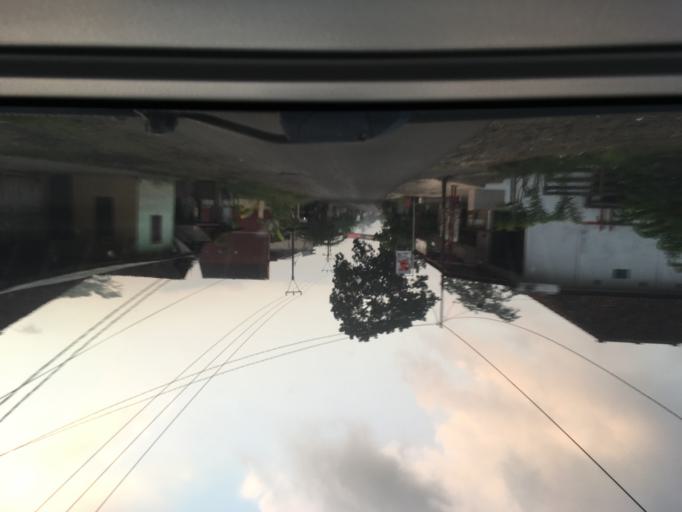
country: ID
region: West Java
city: Padamulya
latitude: -7.2058
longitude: 108.1996
